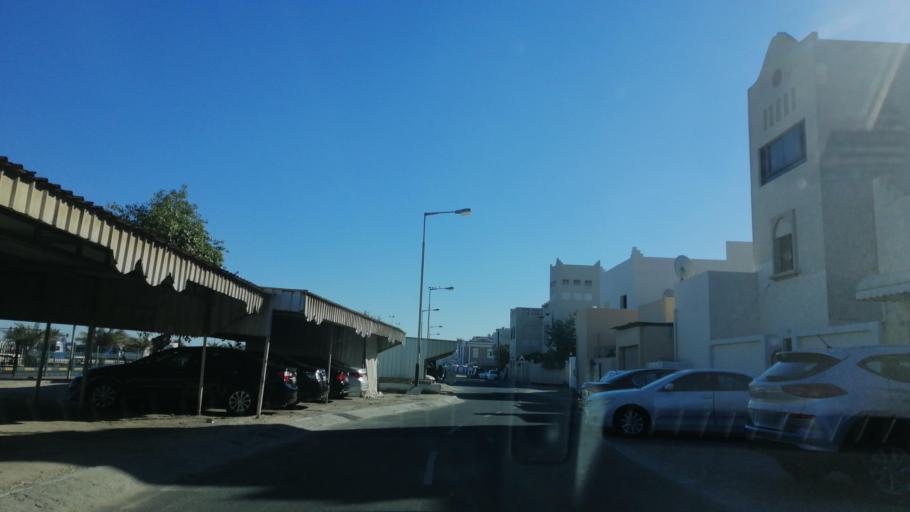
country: BH
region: Muharraq
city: Al Hadd
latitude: 26.2469
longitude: 50.6572
